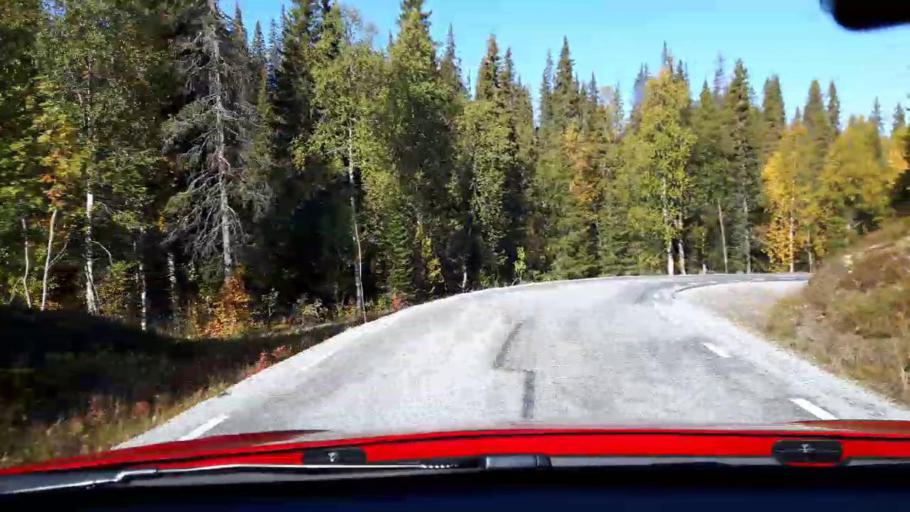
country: NO
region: Nord-Trondelag
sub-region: Lierne
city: Sandvika
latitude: 64.6191
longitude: 13.6979
